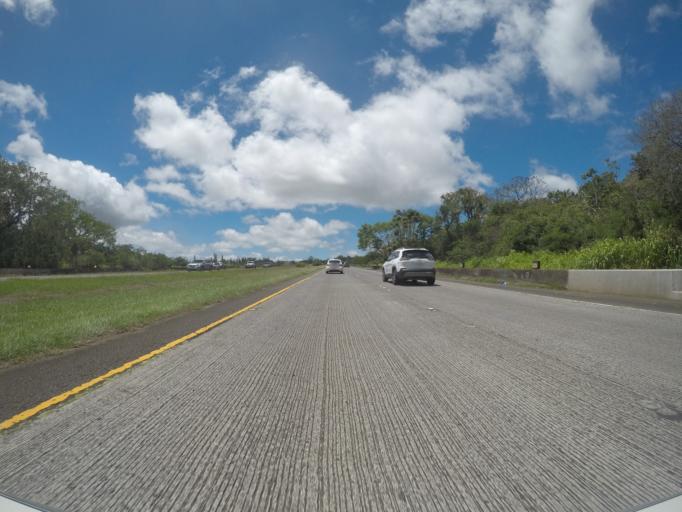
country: US
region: Hawaii
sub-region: Honolulu County
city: Wahiawa
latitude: 21.4836
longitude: -158.0250
